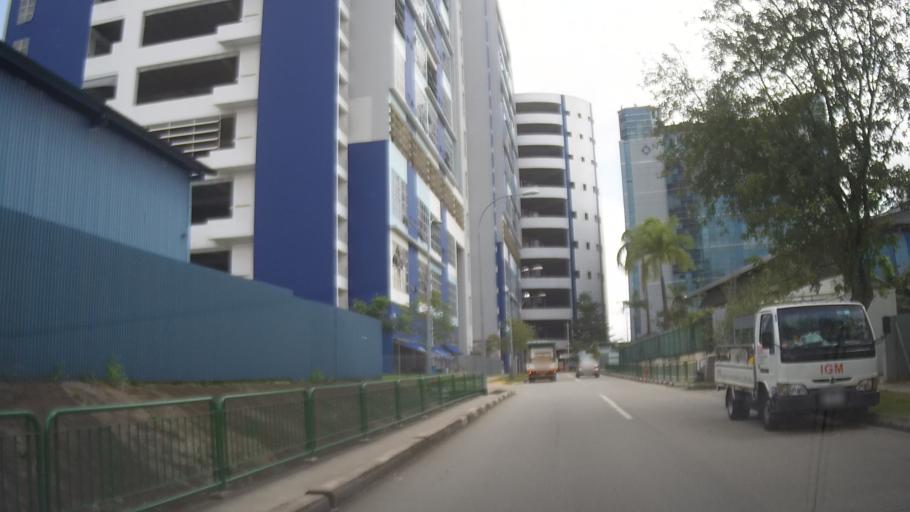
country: MY
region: Johor
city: Johor Bahru
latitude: 1.4080
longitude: 103.7587
